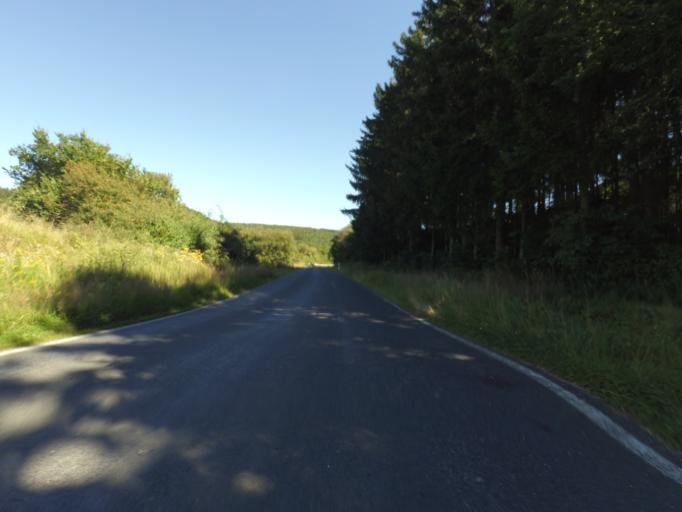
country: DE
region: Rheinland-Pfalz
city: Nohn
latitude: 50.3114
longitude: 6.7769
